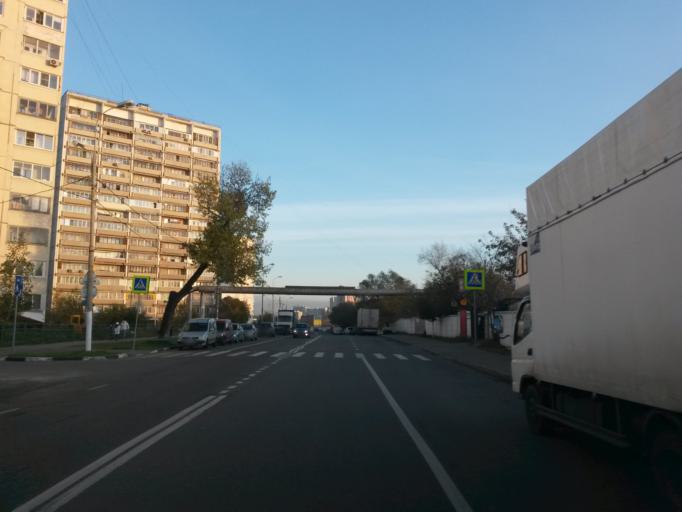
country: RU
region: Moskovskaya
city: Shcherbinka
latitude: 55.5386
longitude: 37.5738
